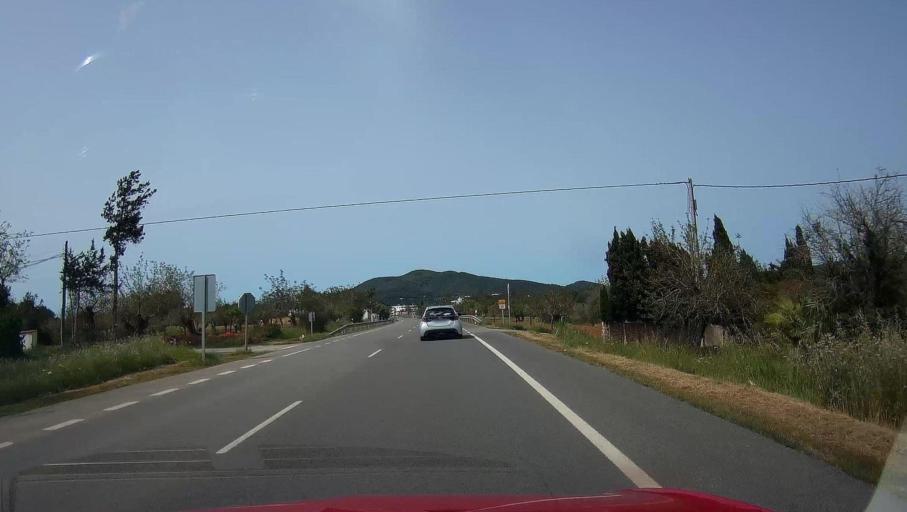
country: ES
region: Balearic Islands
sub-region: Illes Balears
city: Sant Joan de Labritja
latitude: 39.0462
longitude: 1.4915
